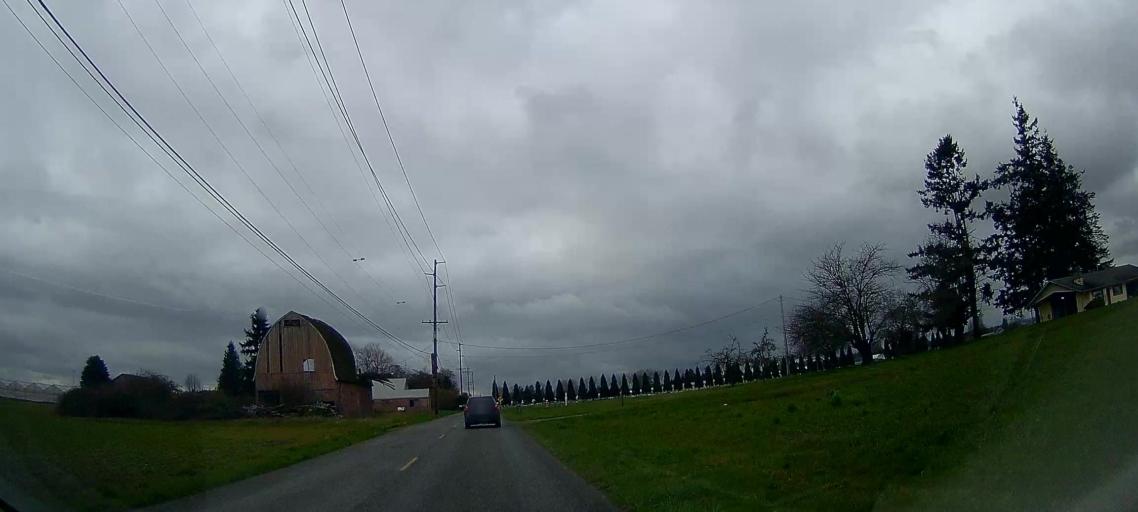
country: US
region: Washington
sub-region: Skagit County
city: Mount Vernon
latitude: 48.4433
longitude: -122.3527
